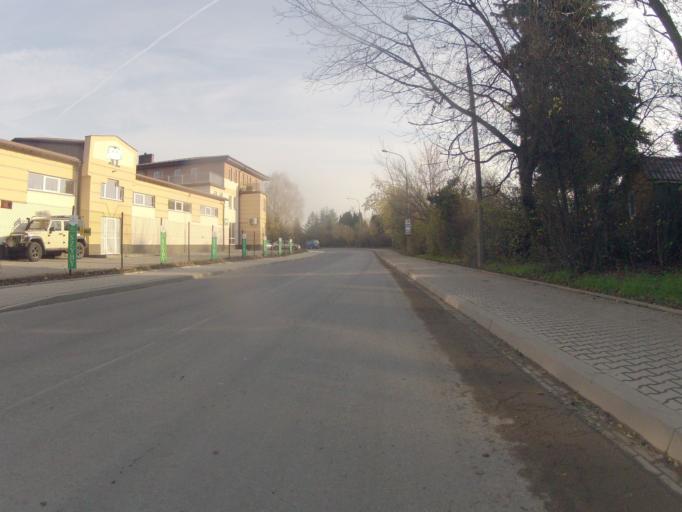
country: PL
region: Lesser Poland Voivodeship
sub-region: Krakow
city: Krakow
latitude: 50.0507
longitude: 19.9787
